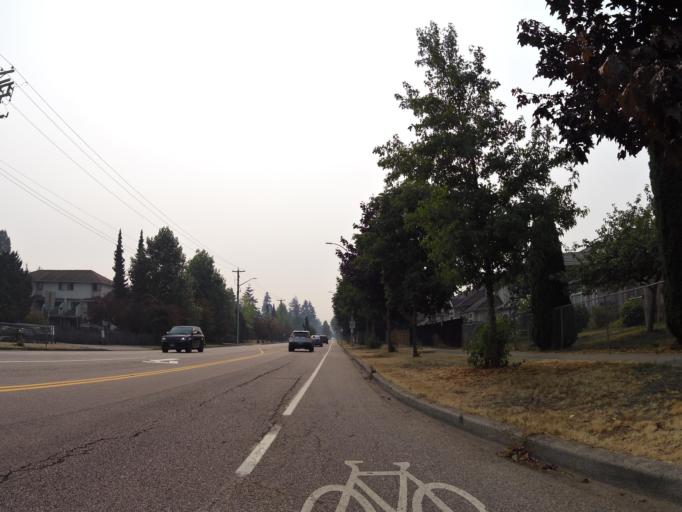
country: CA
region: British Columbia
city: Surrey
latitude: 49.1333
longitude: -122.8567
